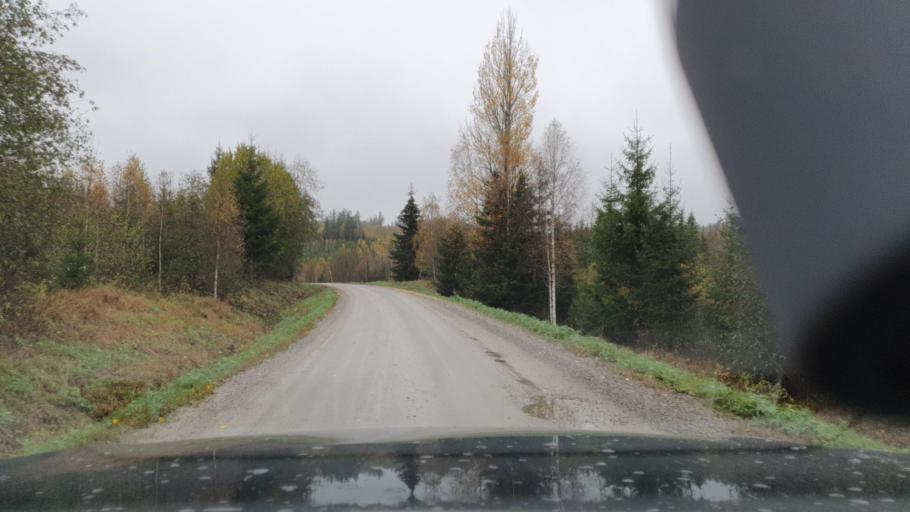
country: SE
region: Vaermland
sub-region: Arvika Kommun
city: Arvika
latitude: 59.8354
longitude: 12.7470
